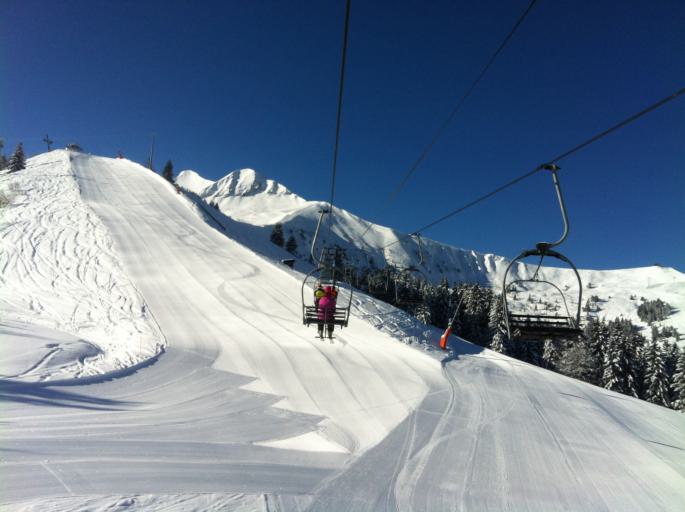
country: FR
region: Rhone-Alpes
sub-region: Departement de la Haute-Savoie
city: Les Contamines-Montjoie
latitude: 45.8523
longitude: 6.7067
